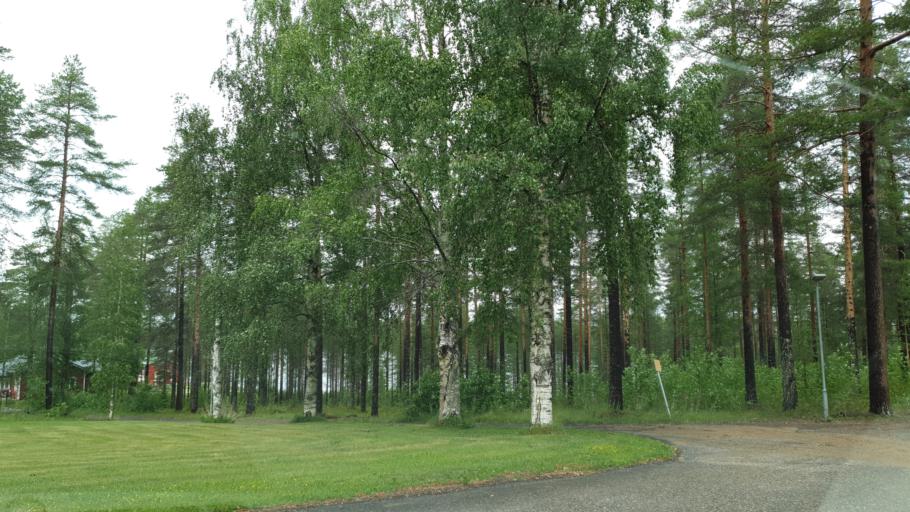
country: FI
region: Kainuu
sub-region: Kehys-Kainuu
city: Kuhmo
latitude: 64.0949
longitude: 29.4348
